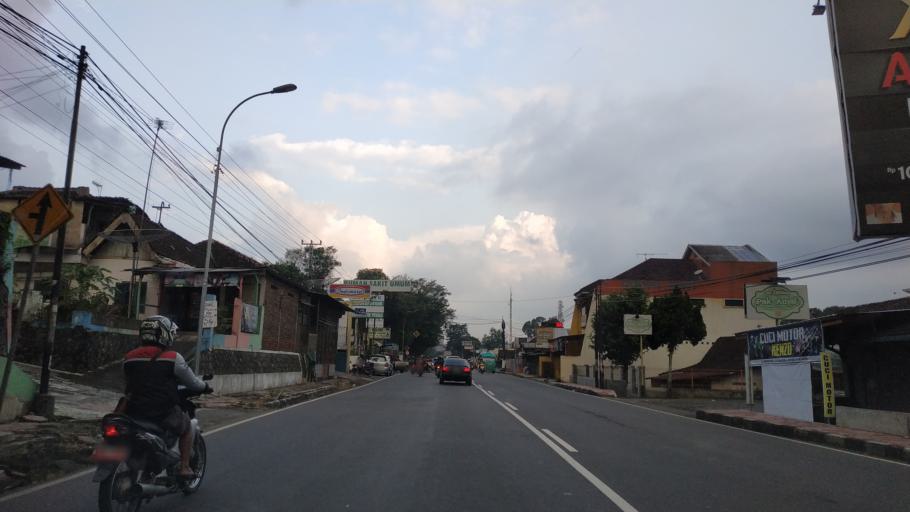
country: ID
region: Central Java
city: Salatiga
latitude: -7.3097
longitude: 110.4903
